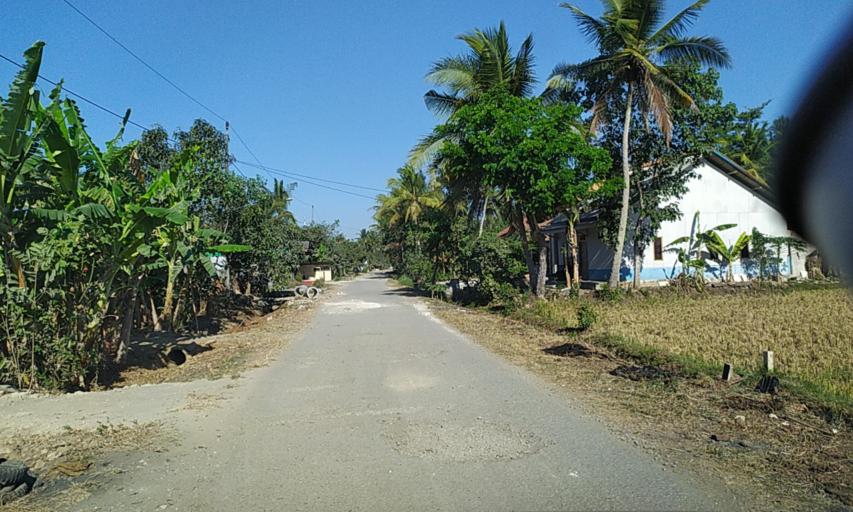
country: ID
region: Central Java
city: Kalenaren
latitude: -7.5808
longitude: 108.7997
